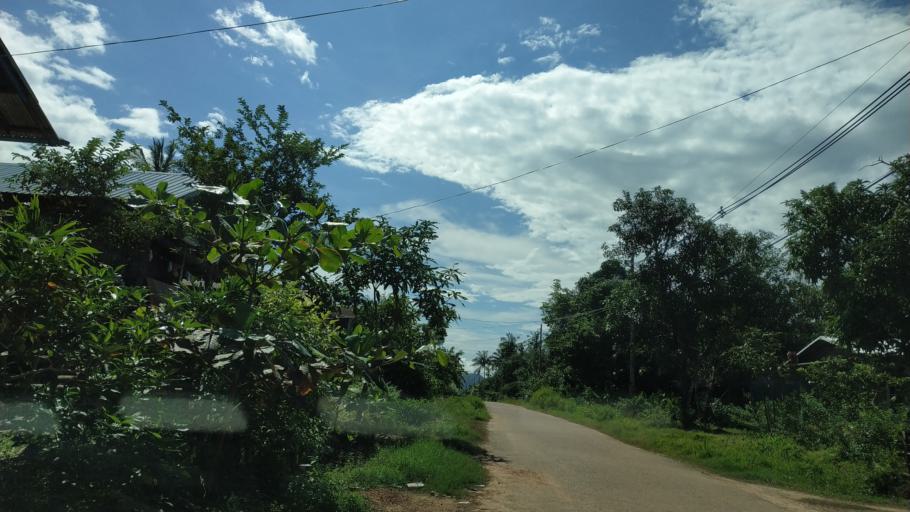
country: MM
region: Tanintharyi
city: Dawei
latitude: 14.1910
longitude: 98.1856
